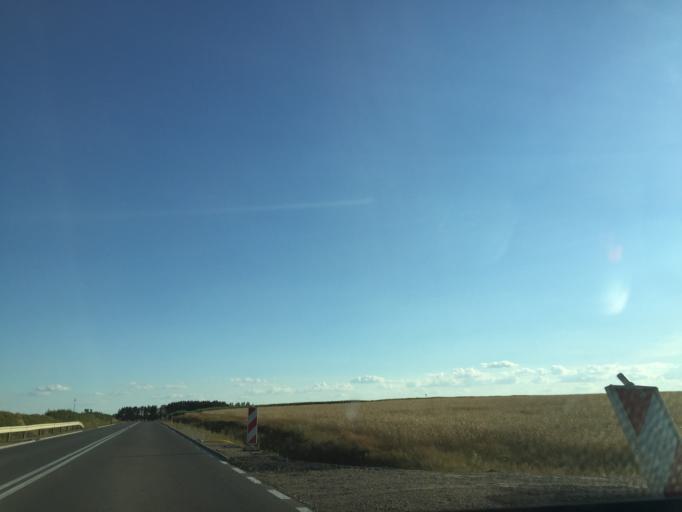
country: PL
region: Podlasie
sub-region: Powiat kolnenski
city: Stawiski
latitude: 53.4778
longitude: 22.2106
